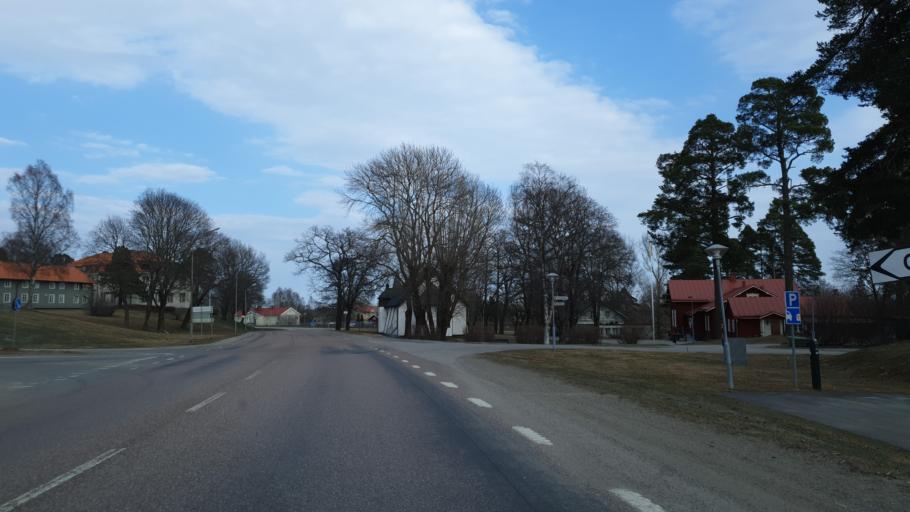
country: SE
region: Gaevleborg
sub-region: Hudiksvalls Kommun
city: Iggesund
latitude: 61.6408
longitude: 17.0744
